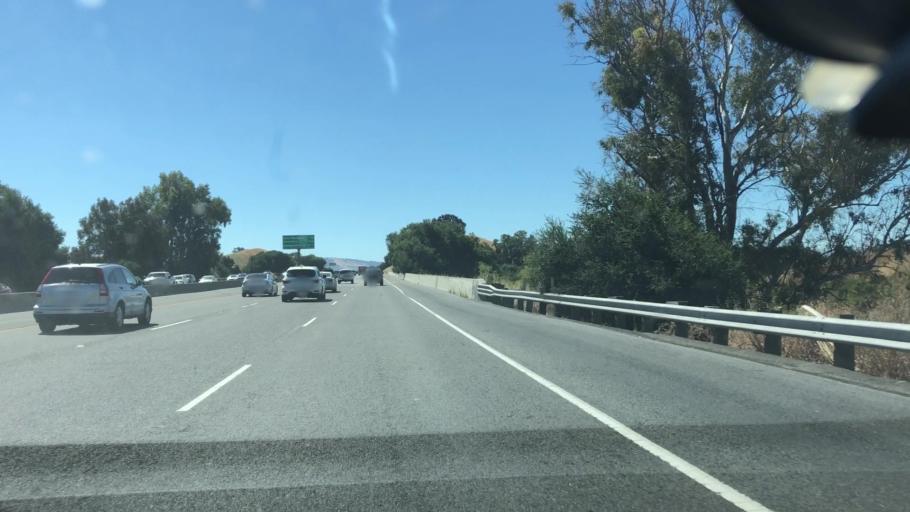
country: US
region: California
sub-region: Alameda County
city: Pleasanton
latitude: 37.6488
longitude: -121.8934
